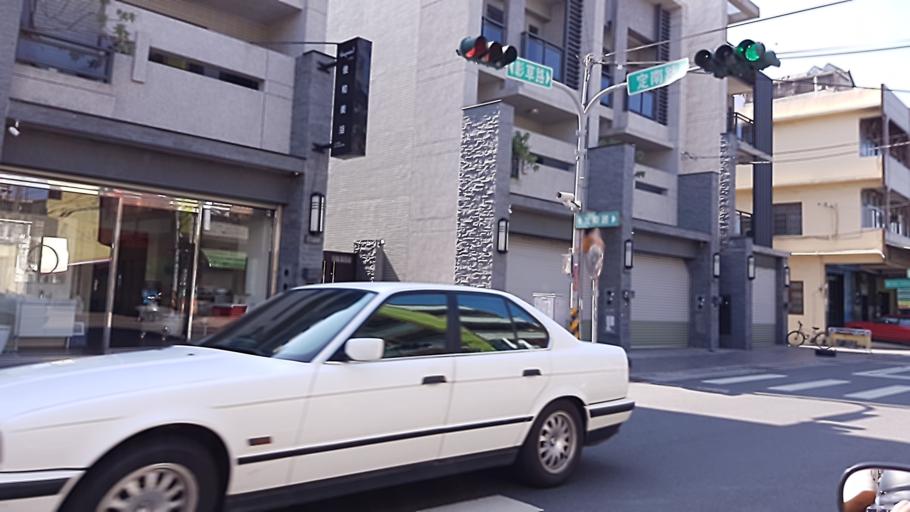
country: TW
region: Taiwan
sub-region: Changhua
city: Chang-hua
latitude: 24.0817
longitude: 120.5096
